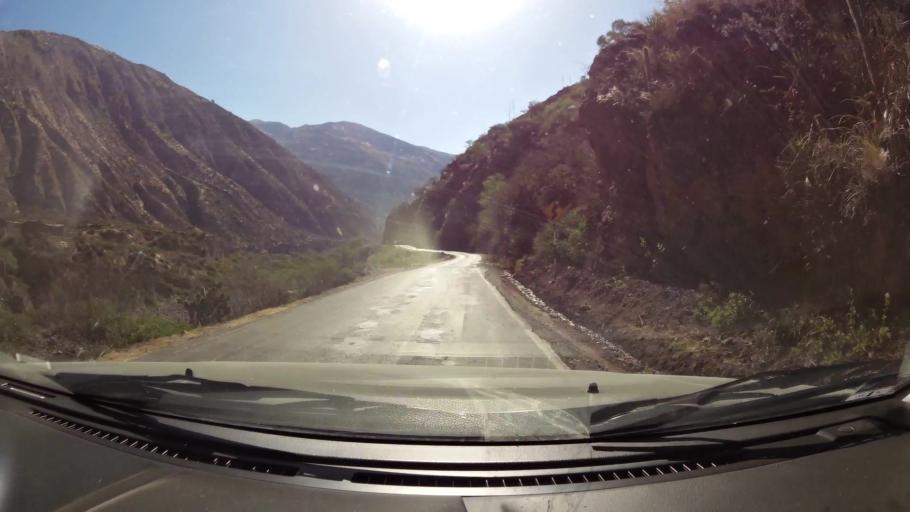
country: PE
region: Huancavelica
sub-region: Provincia de Acobamba
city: Pomacocha
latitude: -12.7618
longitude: -74.5220
